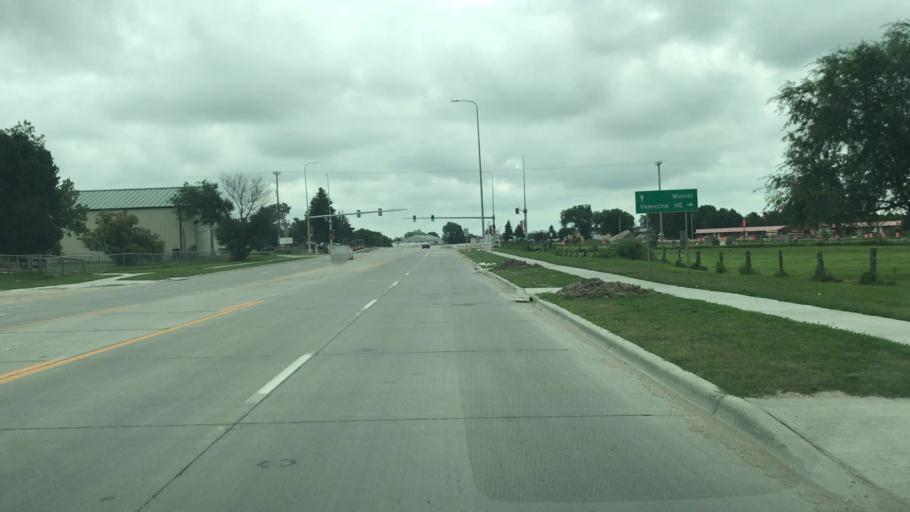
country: US
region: South Dakota
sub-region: Todd County
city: Mission
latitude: 43.3057
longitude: -100.6545
